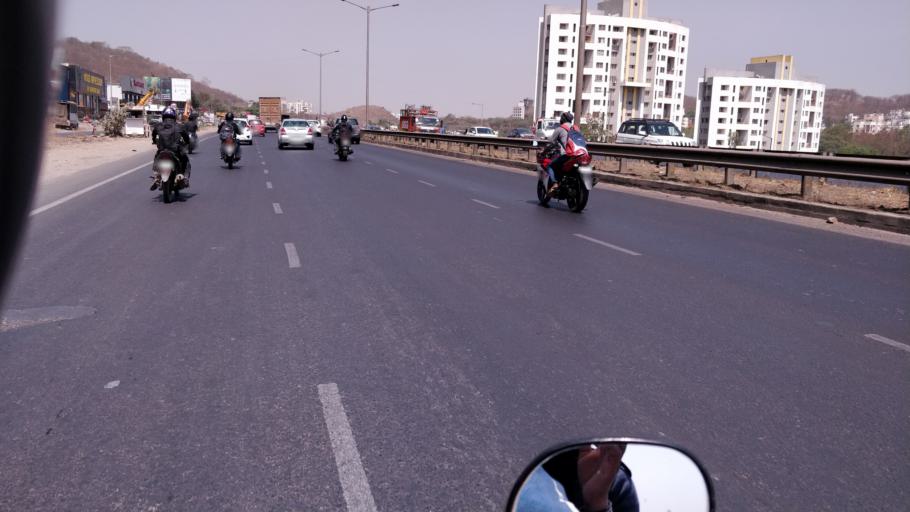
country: IN
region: Maharashtra
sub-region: Pune Division
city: Shivaji Nagar
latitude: 18.5409
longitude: 73.7791
